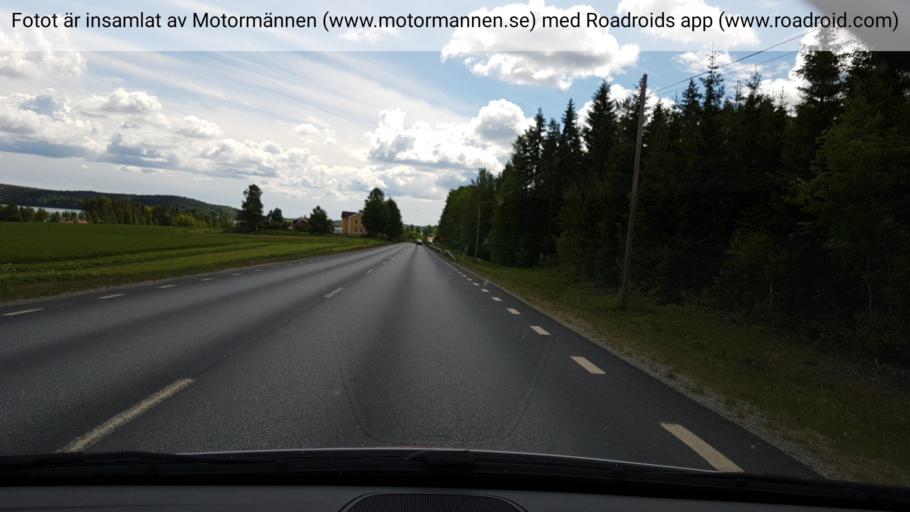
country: SE
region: Vaesterbotten
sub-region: Vannas Kommun
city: Vannasby
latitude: 64.0305
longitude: 20.0172
